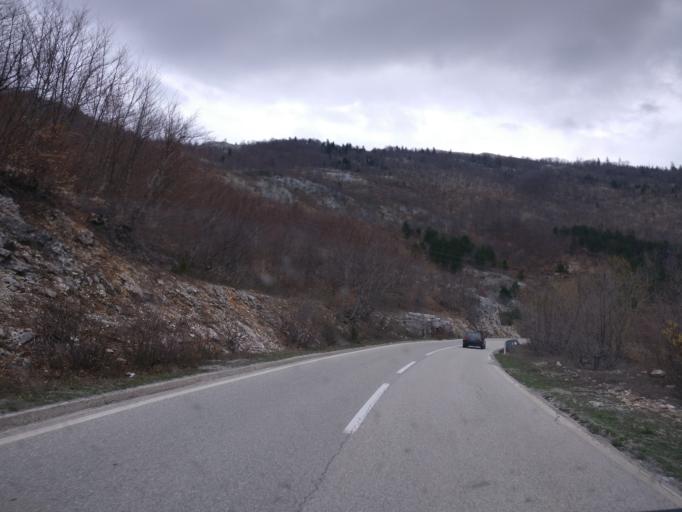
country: ME
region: Opstina Niksic
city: Niksic
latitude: 42.9380
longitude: 18.9291
